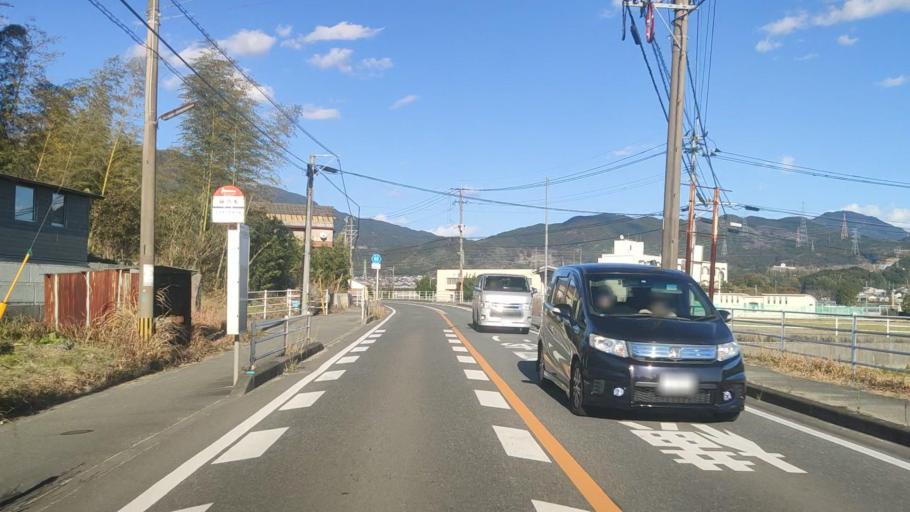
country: JP
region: Fukuoka
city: Dazaifu
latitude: 33.4983
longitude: 130.5482
